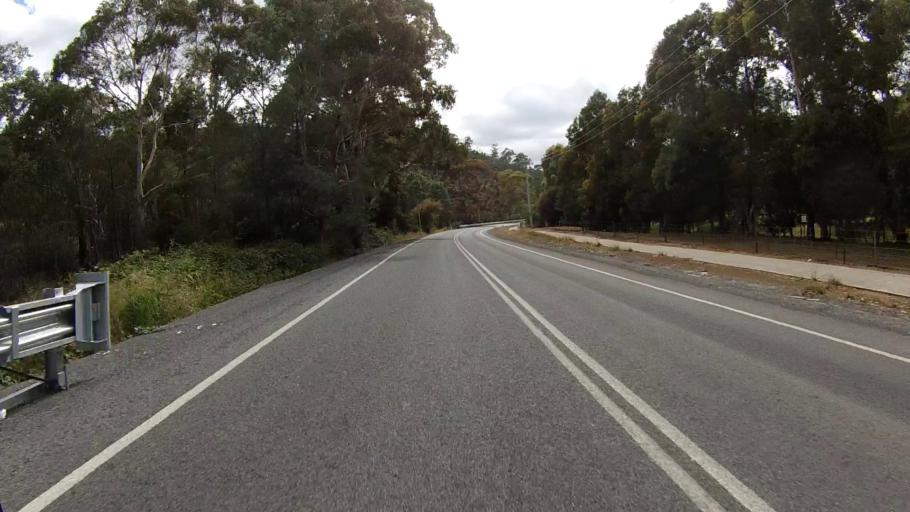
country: AU
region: Tasmania
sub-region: Glenorchy
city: Lutana
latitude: -42.8087
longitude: 147.3376
